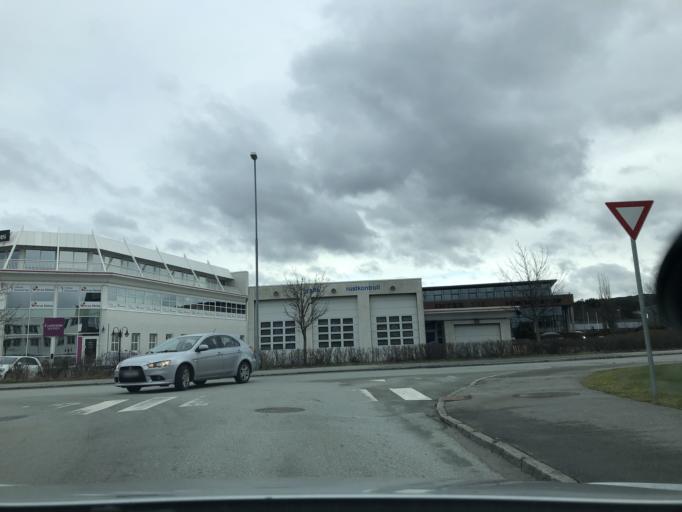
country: NO
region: Rogaland
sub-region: Sandnes
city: Sandnes
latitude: 58.8851
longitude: 5.7244
